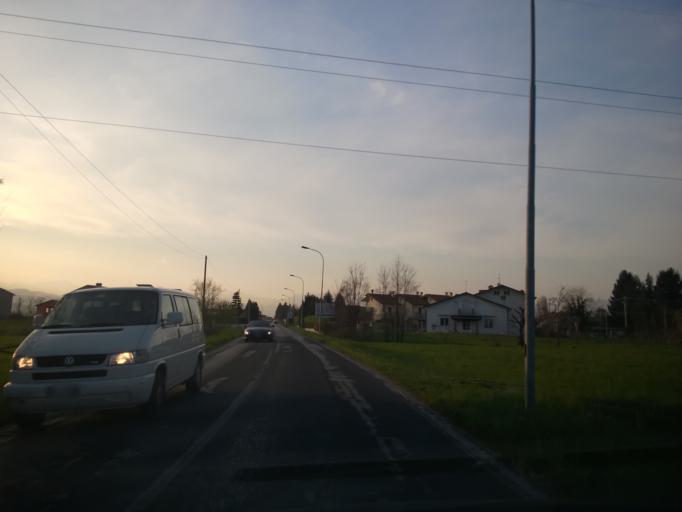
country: IT
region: Veneto
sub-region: Provincia di Vicenza
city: Caldogno-Rettorgole-Cresole
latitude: 45.6028
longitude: 11.5171
